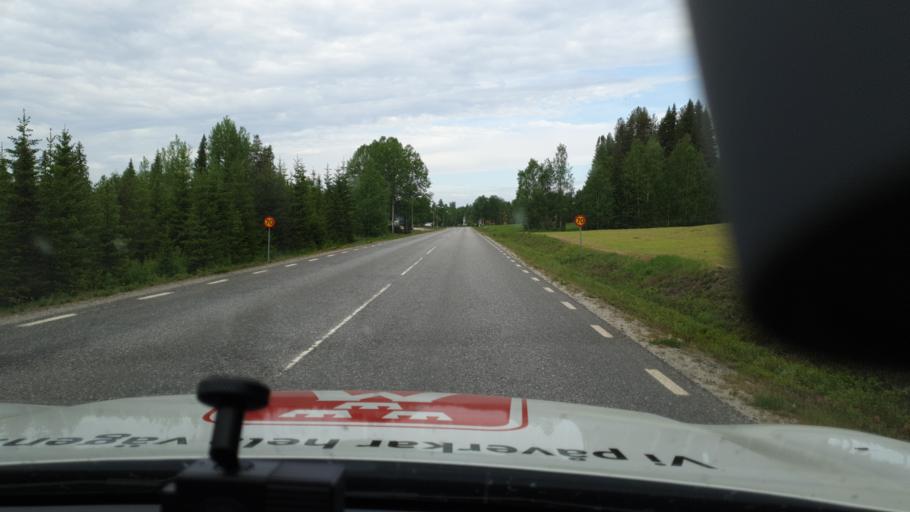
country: SE
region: Vaesterbotten
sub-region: Mala Kommun
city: Mala
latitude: 64.9850
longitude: 18.5356
